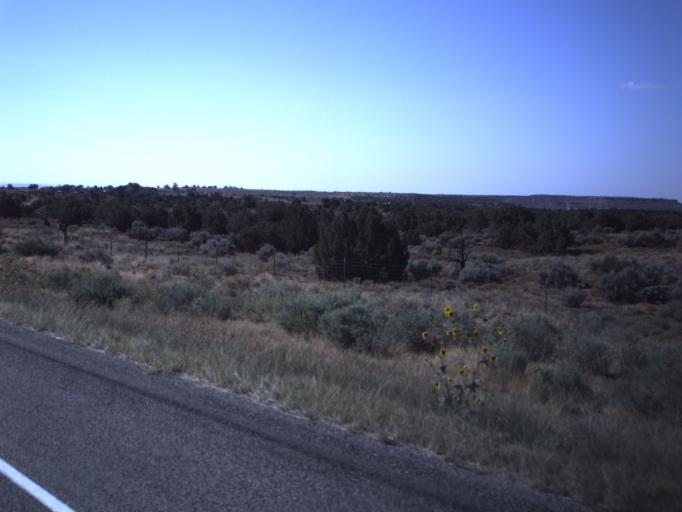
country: US
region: Utah
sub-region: San Juan County
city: Blanding
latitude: 37.4784
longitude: -109.4683
